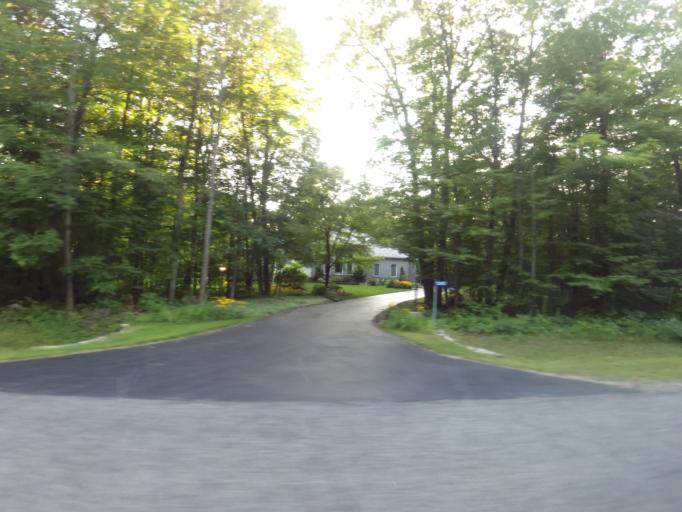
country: CA
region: Ontario
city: Clarence-Rockland
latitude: 45.5009
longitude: -75.4312
